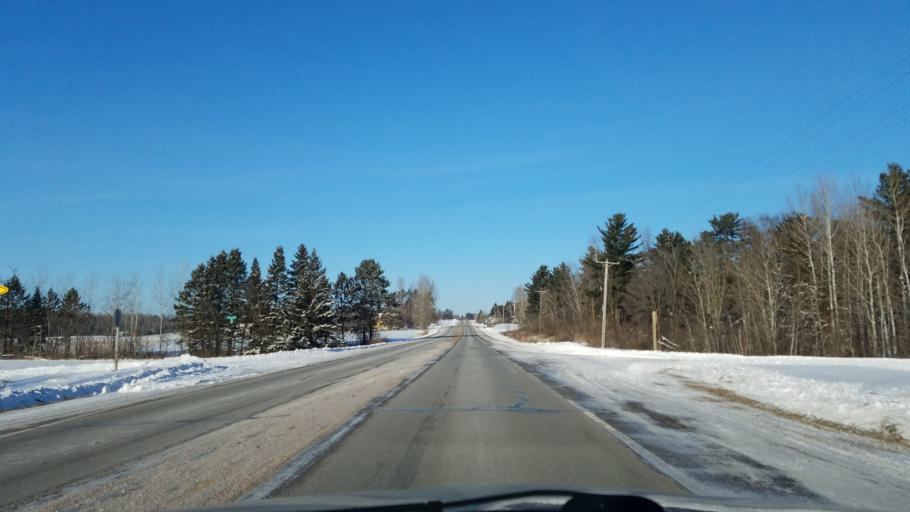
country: US
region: Wisconsin
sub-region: Barron County
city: Cumberland
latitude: 45.5093
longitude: -92.0522
